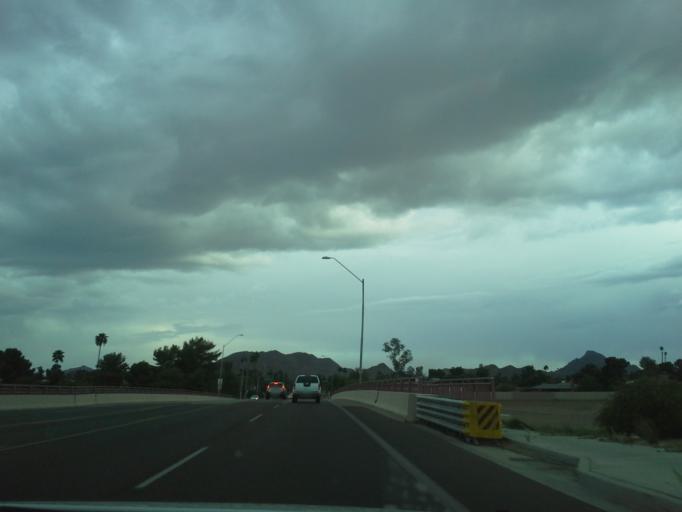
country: US
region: Arizona
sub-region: Maricopa County
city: Paradise Valley
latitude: 33.5986
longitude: -111.9959
